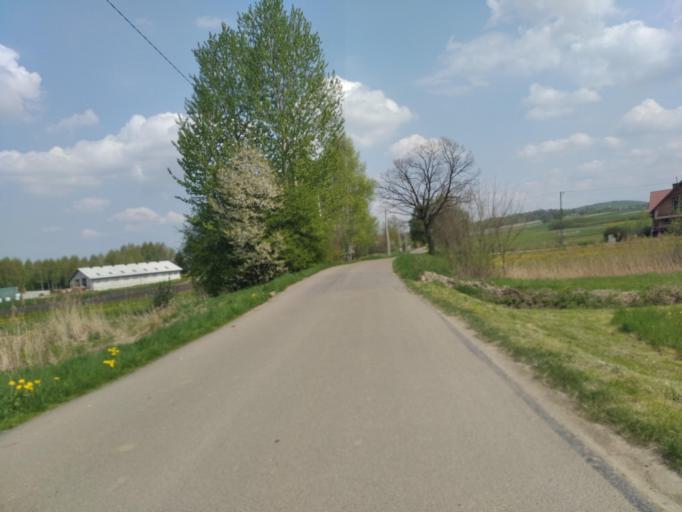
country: PL
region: Subcarpathian Voivodeship
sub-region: Powiat brzozowski
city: Jasionow
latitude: 49.6446
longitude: 21.9803
